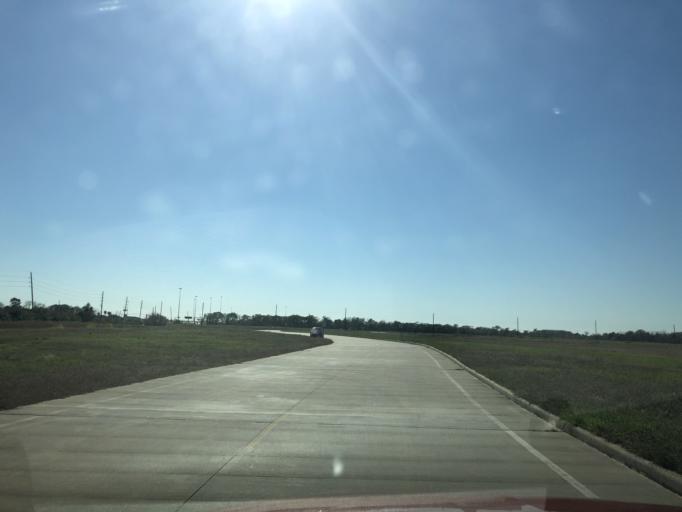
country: US
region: Texas
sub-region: Brazoria County
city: Brookside Village
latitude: 29.5919
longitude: -95.3878
